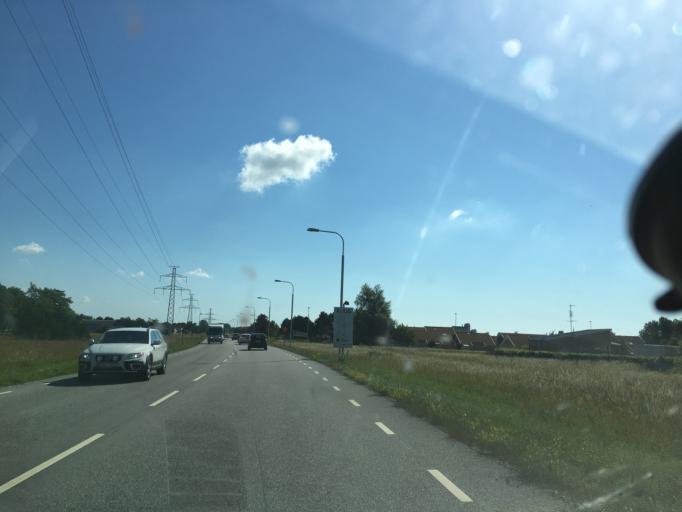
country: SE
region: Skane
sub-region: Kristianstads Kommun
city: Ahus
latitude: 55.9286
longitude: 14.2769
